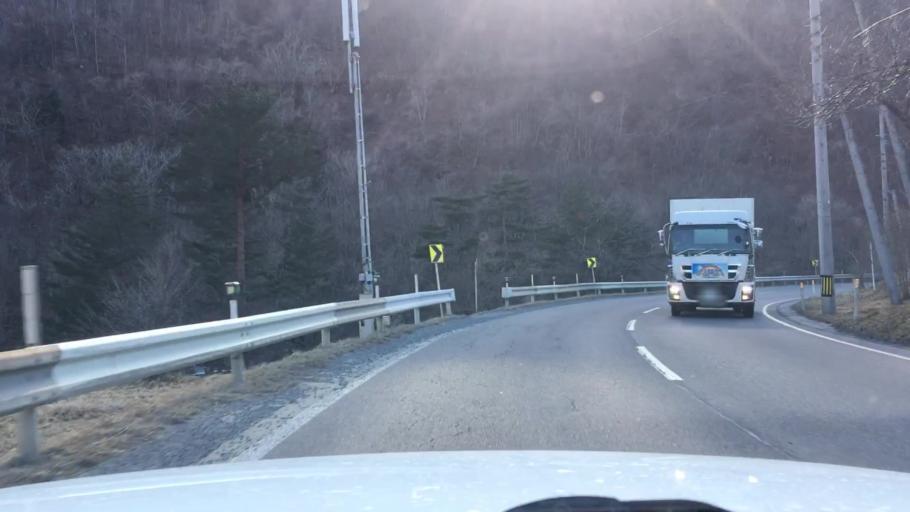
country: JP
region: Iwate
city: Miyako
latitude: 39.6067
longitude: 141.7867
